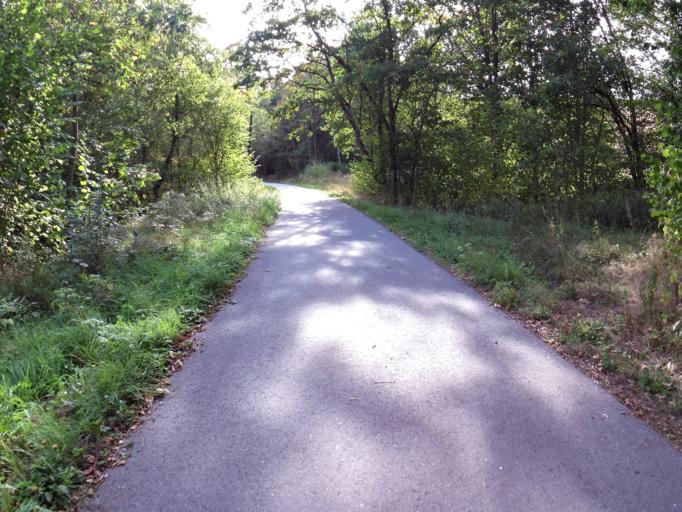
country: DE
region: Rheinland-Pfalz
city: Winterspelt
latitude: 50.2358
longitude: 6.1756
